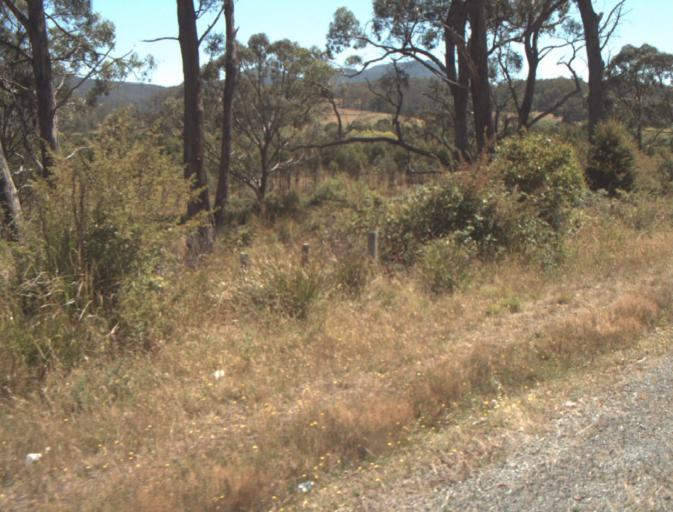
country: AU
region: Tasmania
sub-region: Launceston
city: Newstead
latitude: -41.3749
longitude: 147.3131
